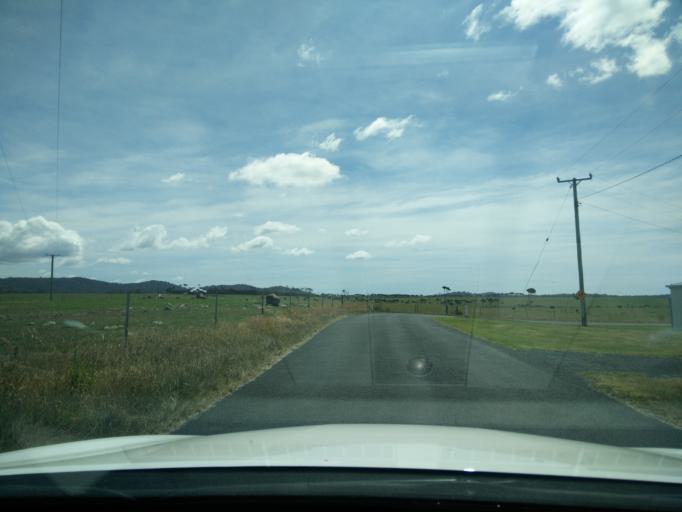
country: AU
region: Tasmania
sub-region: Break O'Day
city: St Helens
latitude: -41.1664
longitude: 148.2828
